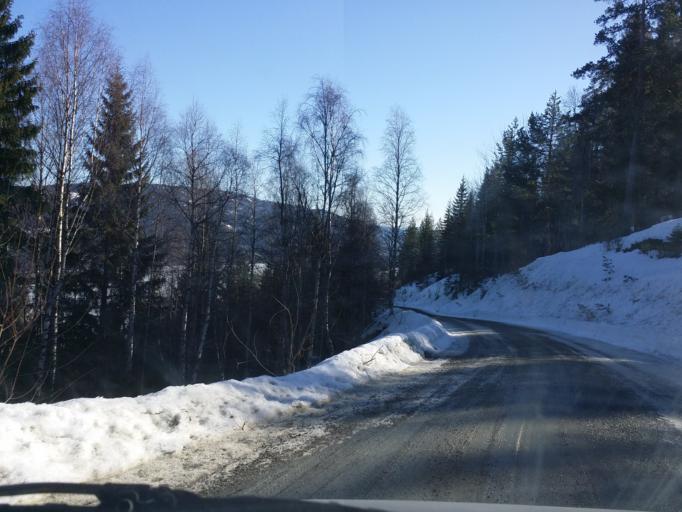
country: NO
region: Buskerud
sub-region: Ringerike
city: Honefoss
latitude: 60.3991
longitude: 10.0358
